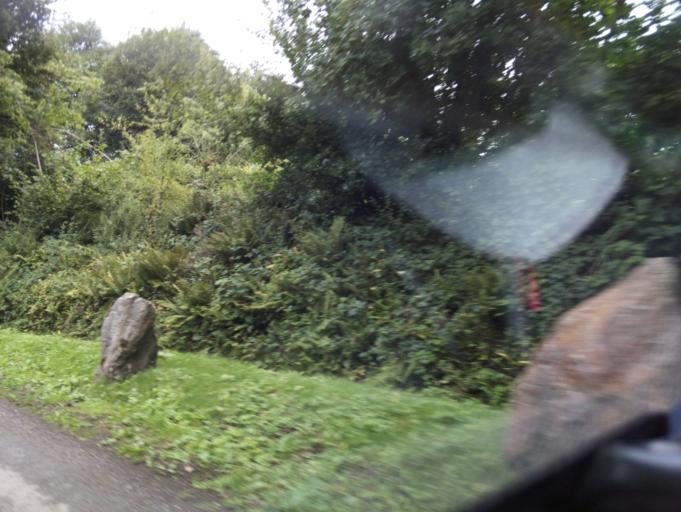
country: GB
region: England
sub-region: Devon
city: Kingsbridge
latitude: 50.2824
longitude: -3.7174
